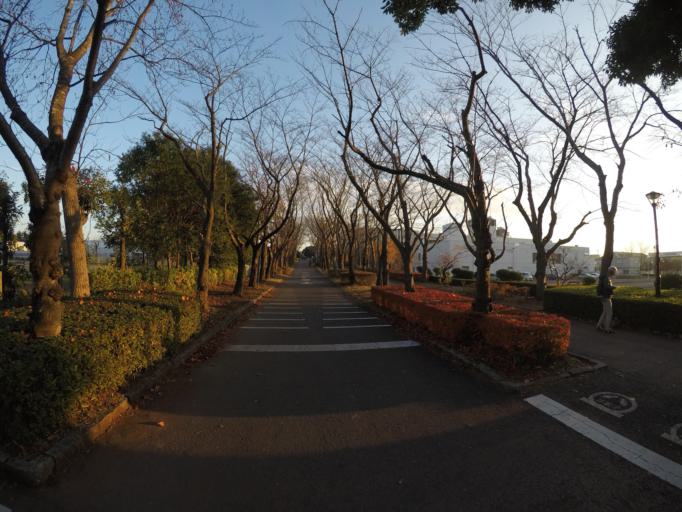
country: JP
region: Ibaraki
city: Naka
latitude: 36.0755
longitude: 140.1180
